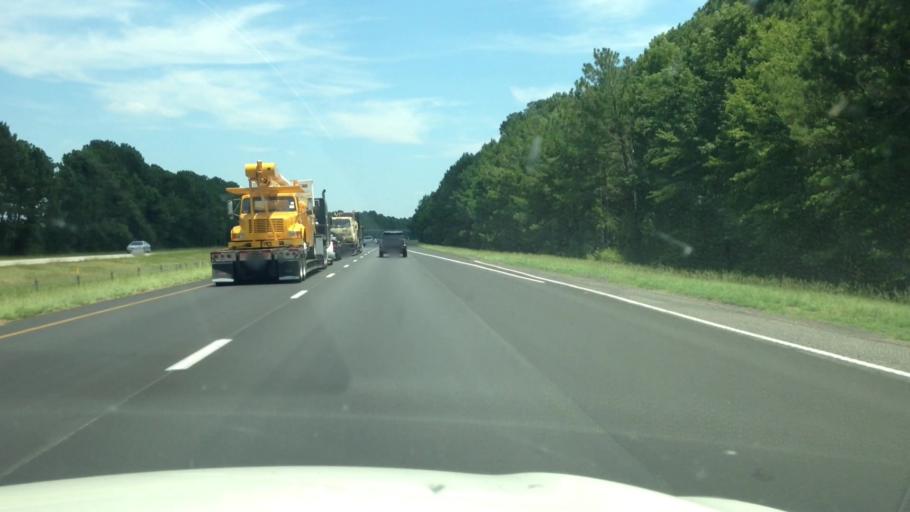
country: US
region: South Carolina
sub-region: Florence County
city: Timmonsville
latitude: 34.2062
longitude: -80.0484
